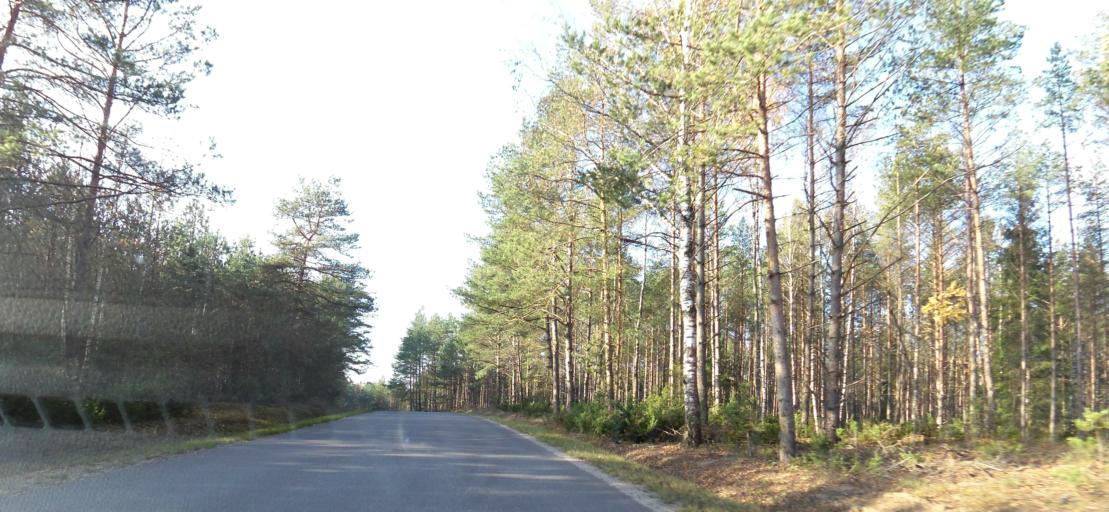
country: LT
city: Trakai
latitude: 54.5308
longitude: 24.9791
